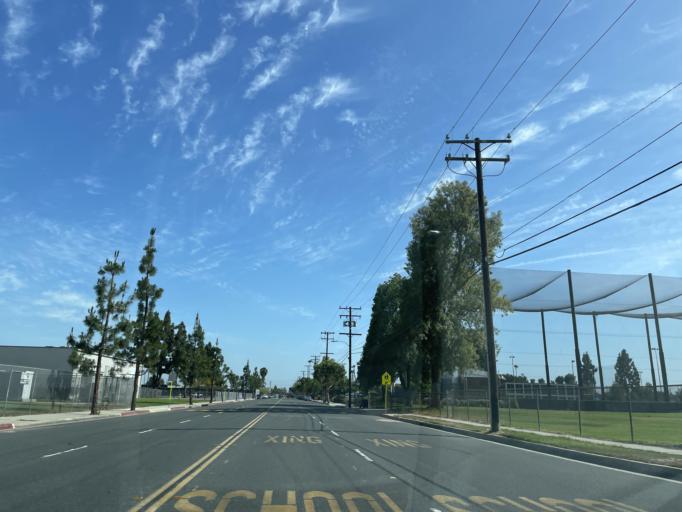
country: US
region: California
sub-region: Los Angeles County
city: Norwalk
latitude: 33.9086
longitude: -118.0554
